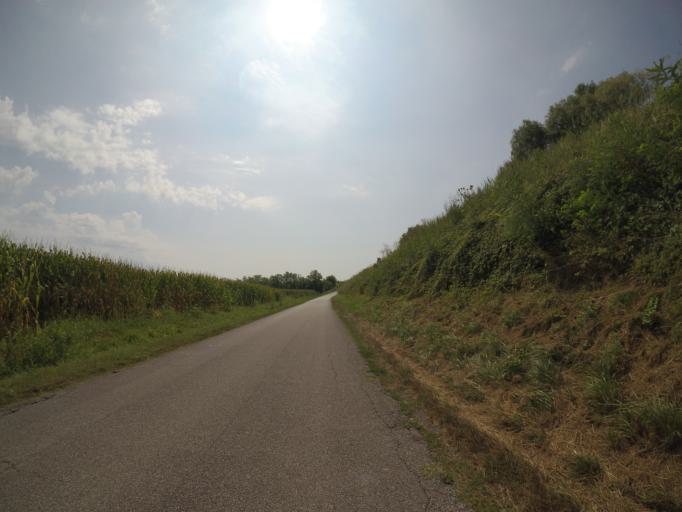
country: IT
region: Friuli Venezia Giulia
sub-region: Provincia di Udine
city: Pertegada
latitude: 45.7006
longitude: 13.0518
